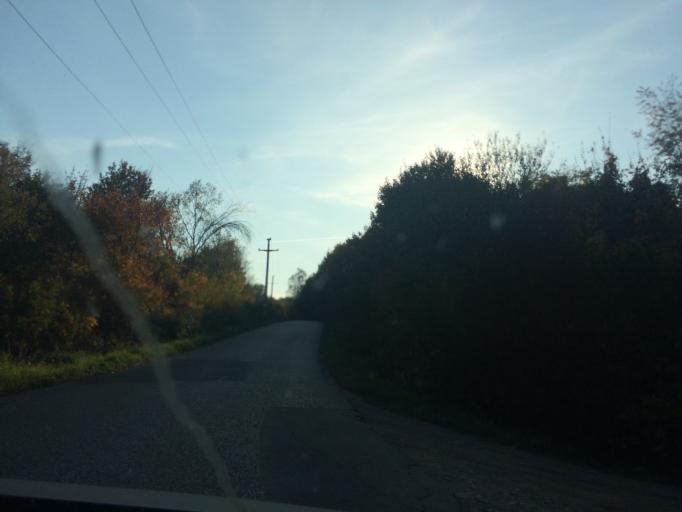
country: RS
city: Stepojevac
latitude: 44.4269
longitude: 20.3956
